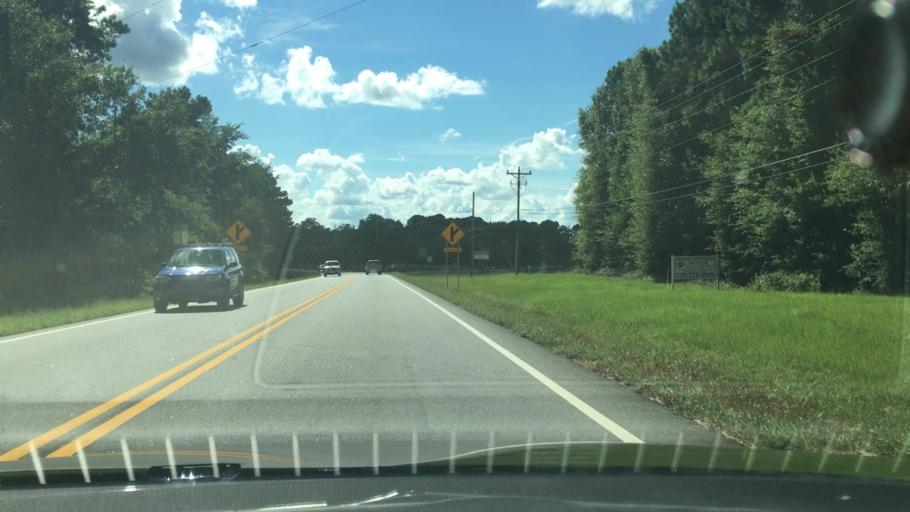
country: US
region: Georgia
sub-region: Butts County
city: Jackson
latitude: 33.2912
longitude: -84.0134
